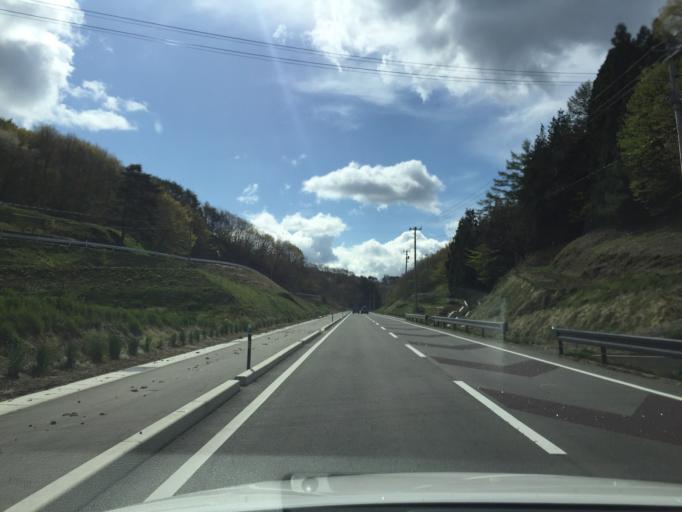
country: JP
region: Fukushima
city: Funehikimachi-funehiki
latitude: 37.6262
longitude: 140.6406
